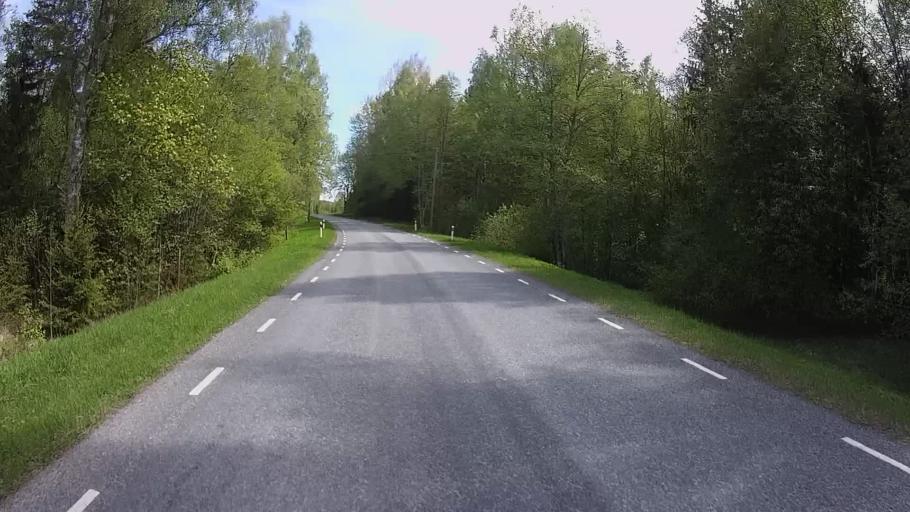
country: EE
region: Valgamaa
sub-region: Valga linn
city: Valga
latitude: 57.6962
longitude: 26.2534
